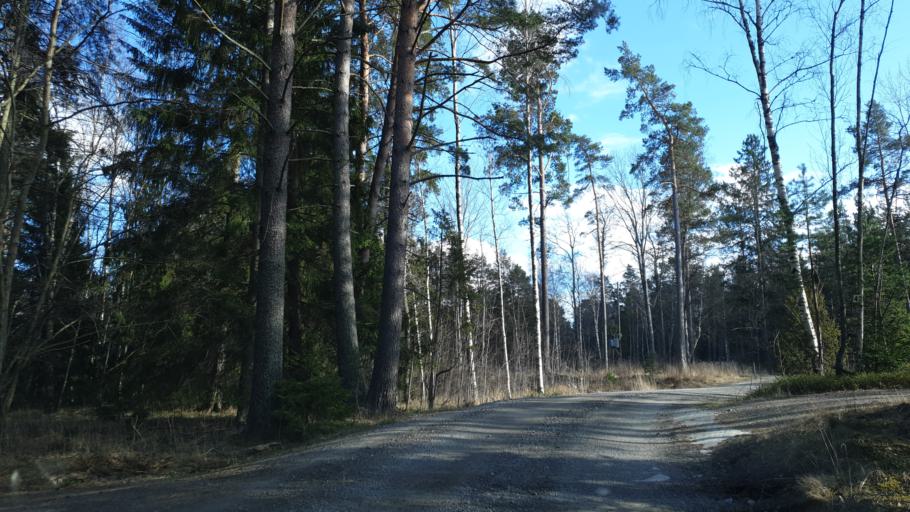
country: SE
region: Stockholm
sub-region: Varmdo Kommun
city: Holo
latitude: 59.2732
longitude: 18.6370
